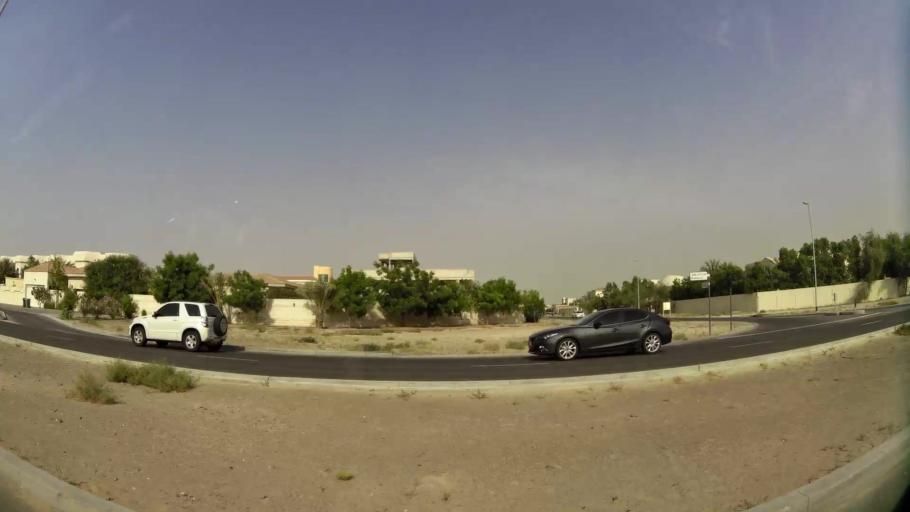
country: AE
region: Ash Shariqah
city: Sharjah
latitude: 25.2528
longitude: 55.4550
